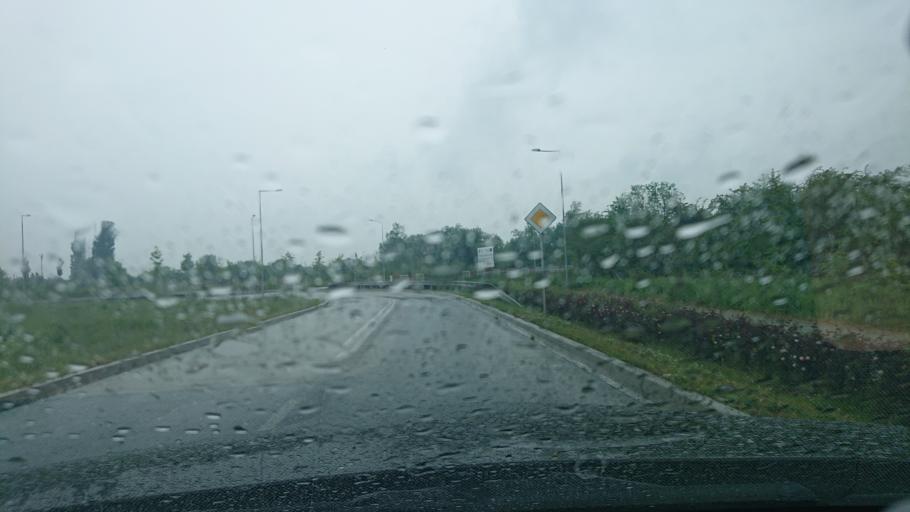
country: PL
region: Greater Poland Voivodeship
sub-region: Powiat gnieznienski
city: Gniezno
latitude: 52.5252
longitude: 17.6247
